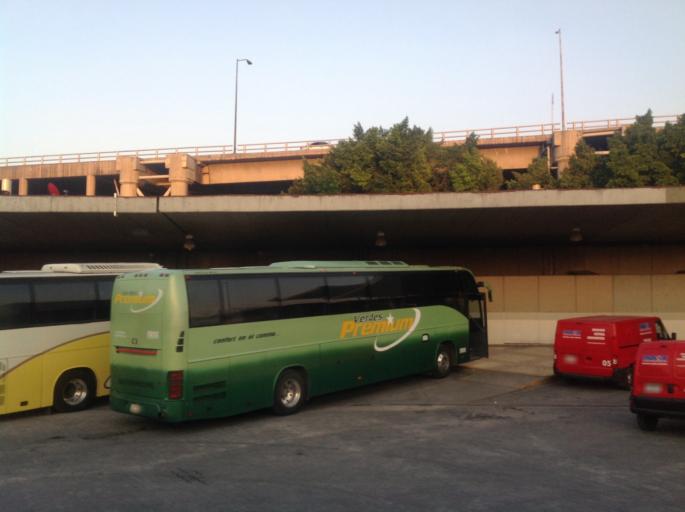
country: MX
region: Mexico City
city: Mexico City
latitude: 19.4303
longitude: -99.1112
